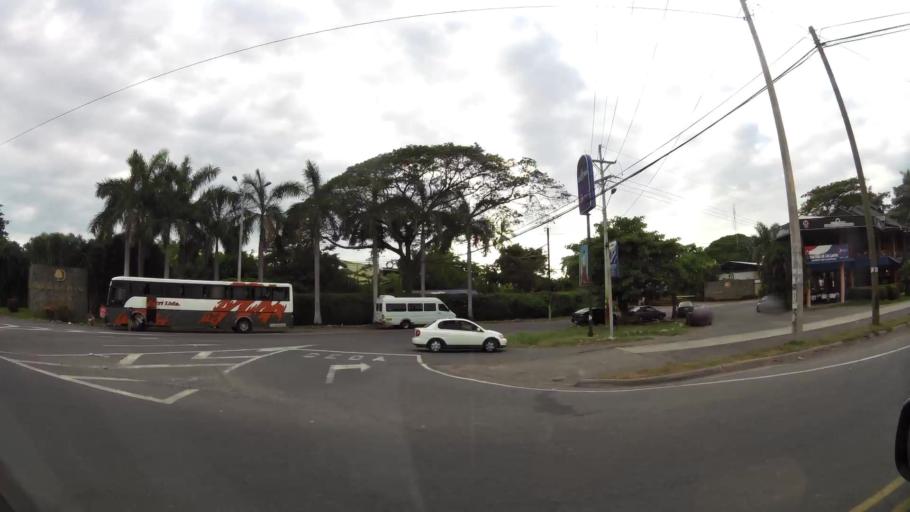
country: CR
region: Puntarenas
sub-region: Canton Central de Puntarenas
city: Chacarita
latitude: 9.9691
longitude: -84.7379
